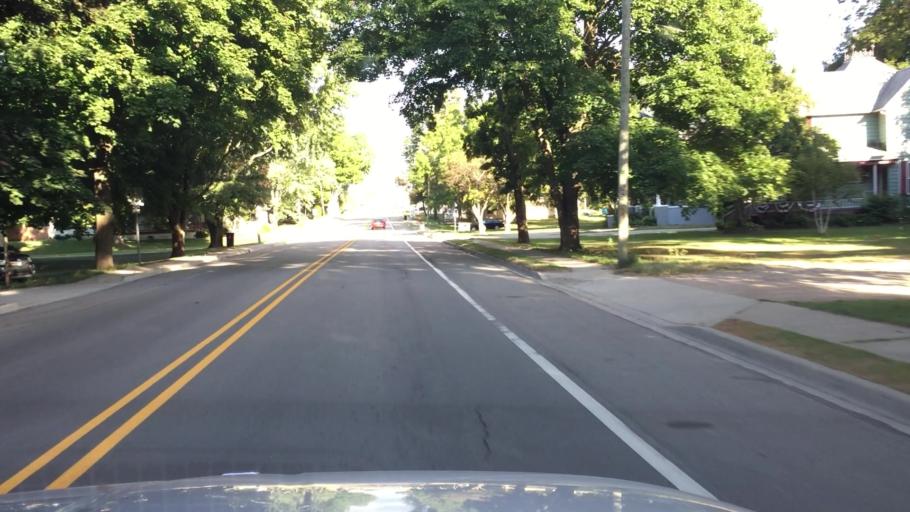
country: US
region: Michigan
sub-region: Saint Clair County
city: Yale
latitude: 43.1248
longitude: -82.7967
